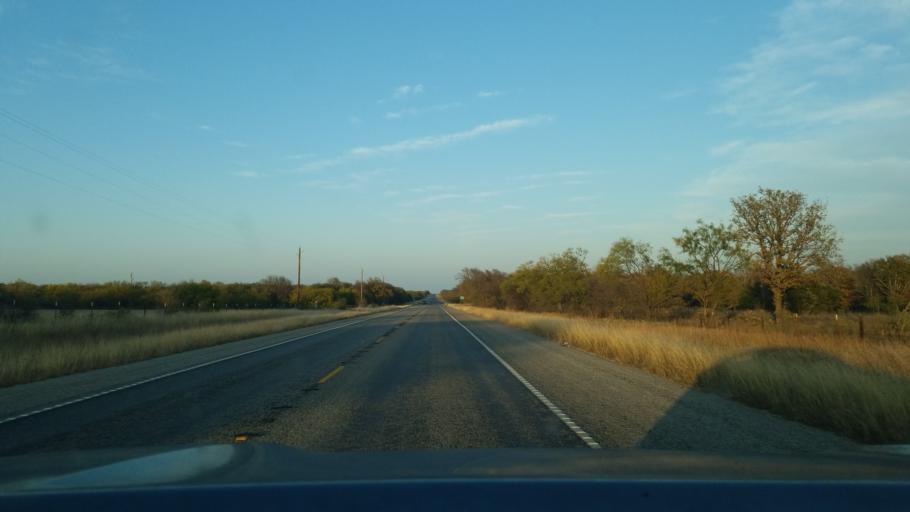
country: US
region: Texas
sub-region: Eastland County
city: Cisco
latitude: 32.4182
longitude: -98.9393
